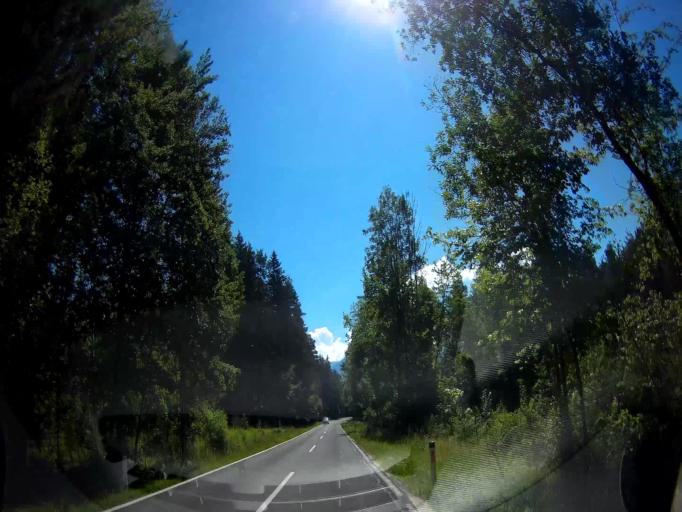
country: AT
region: Carinthia
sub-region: Politischer Bezirk Volkermarkt
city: Gallizien
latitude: 46.5420
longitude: 14.5488
